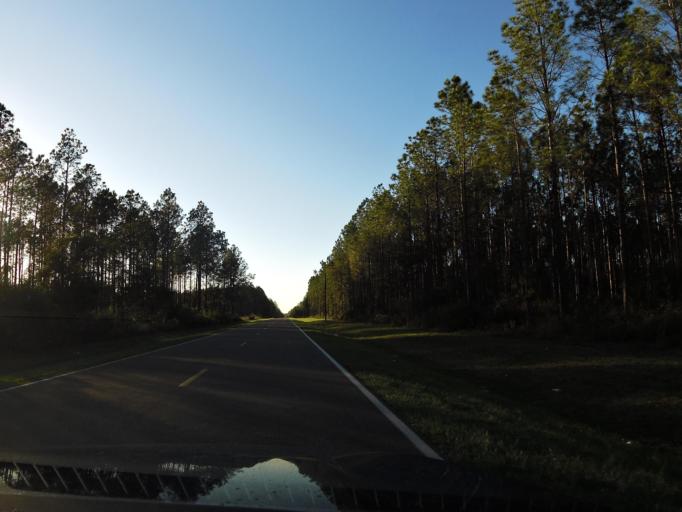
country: US
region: Florida
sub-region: Bradford County
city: Starke
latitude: 29.8530
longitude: -82.0998
